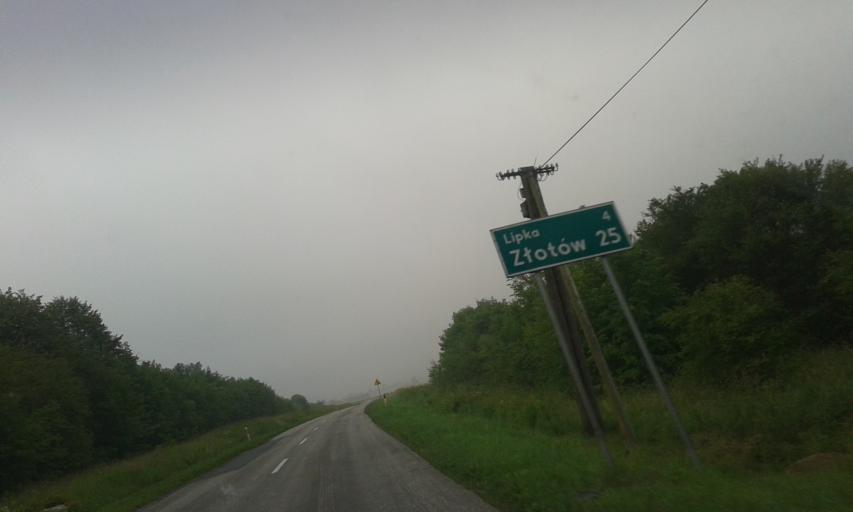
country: PL
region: Pomeranian Voivodeship
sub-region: Powiat czluchowski
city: Debrzno
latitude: 53.5215
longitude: 17.2324
